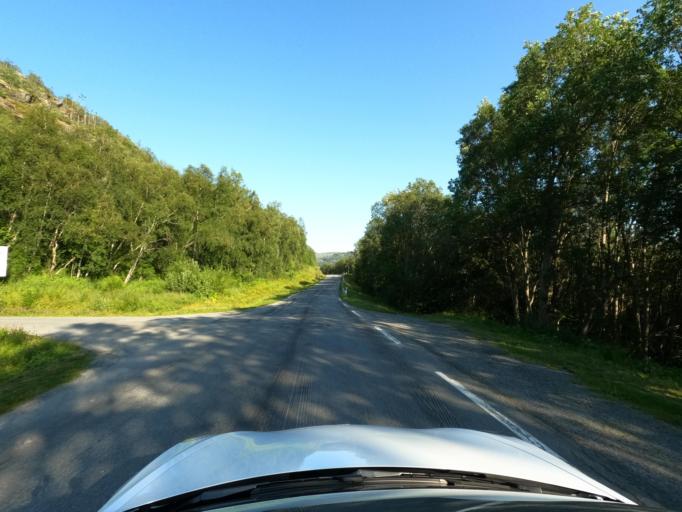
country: NO
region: Nordland
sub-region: Narvik
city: Bjerkvik
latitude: 68.5535
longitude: 17.5744
